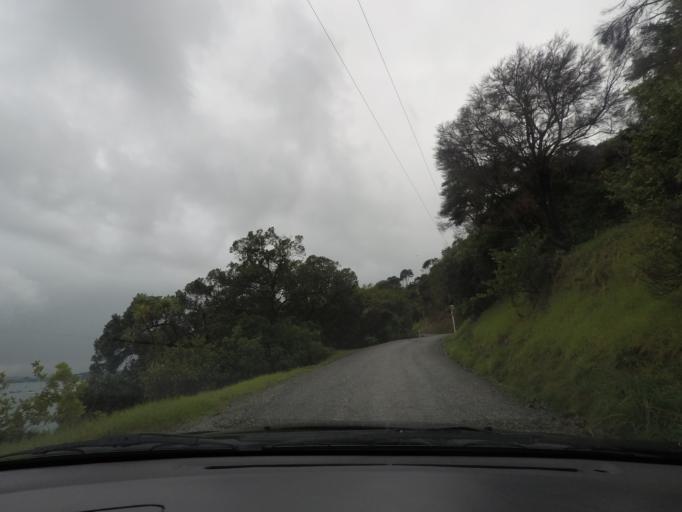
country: NZ
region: Auckland
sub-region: Auckland
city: Warkworth
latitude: -36.4849
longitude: 174.7245
